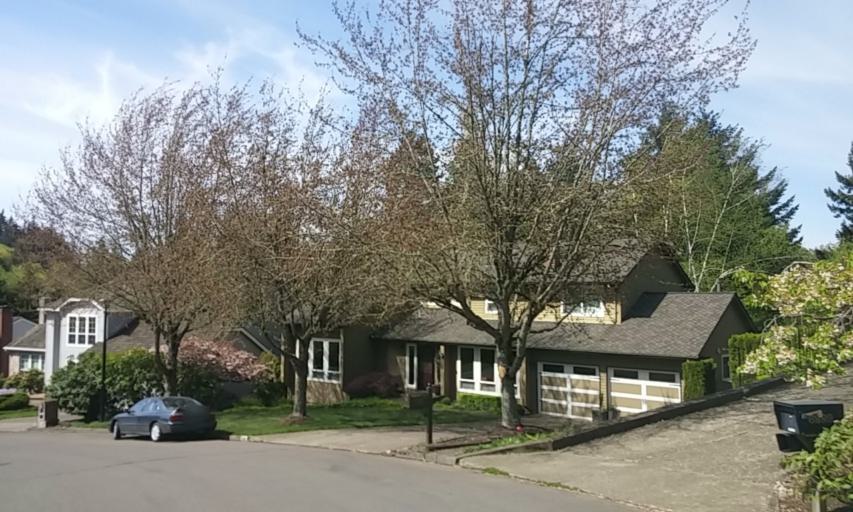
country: US
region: Oregon
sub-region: Washington County
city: West Haven-Sylvan
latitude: 45.5188
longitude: -122.7497
